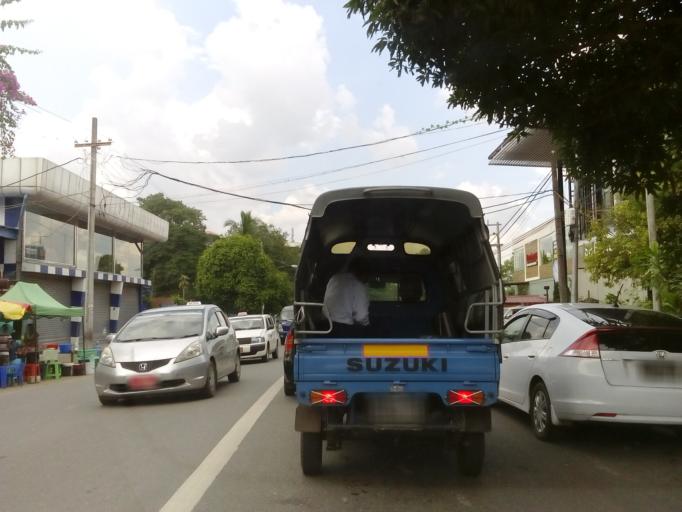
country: MM
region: Yangon
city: Yangon
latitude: 16.8198
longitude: 96.1592
